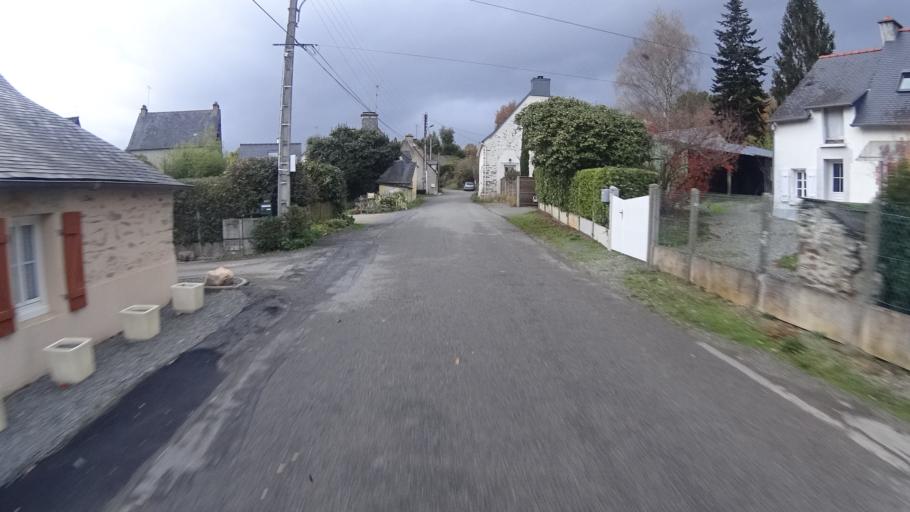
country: FR
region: Pays de la Loire
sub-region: Departement de la Loire-Atlantique
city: Saint-Nicolas-de-Redon
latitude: 47.6572
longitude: -2.0593
